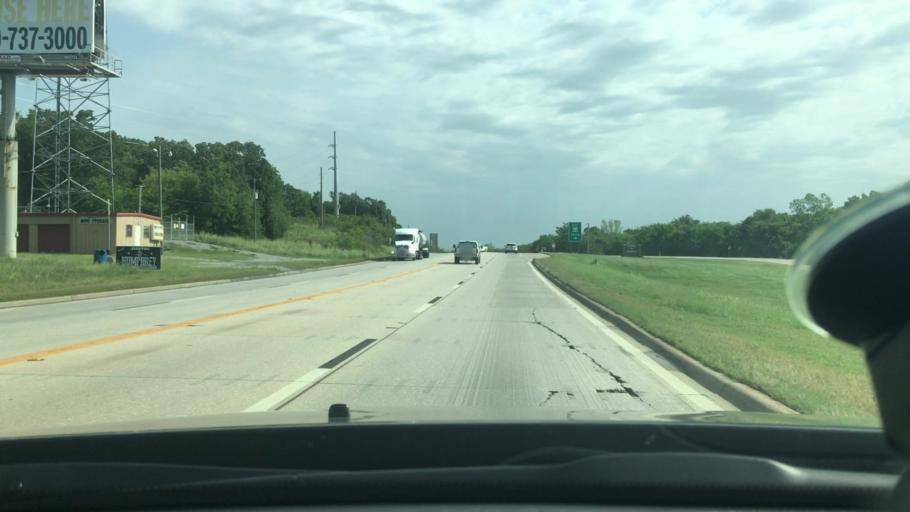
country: US
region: Oklahoma
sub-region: Atoka County
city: Atoka
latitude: 34.4708
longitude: -96.0542
